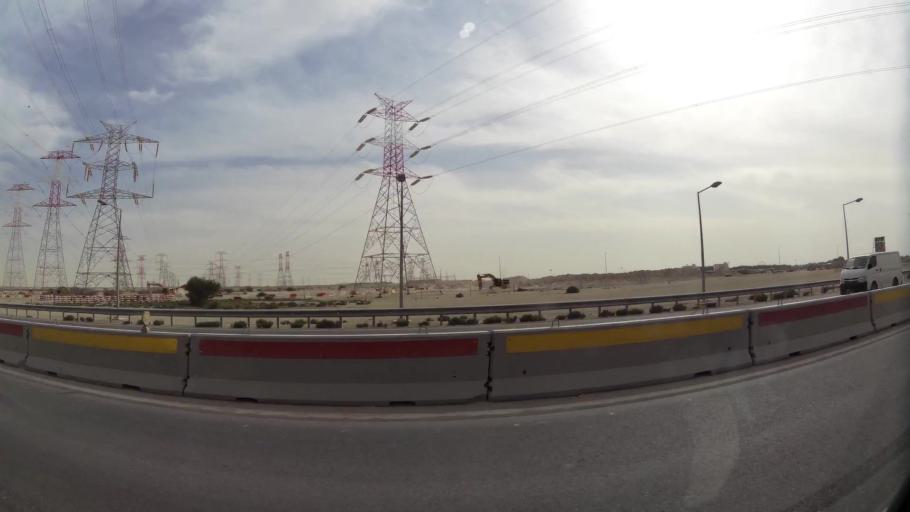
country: QA
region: Baladiyat ar Rayyan
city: Ash Shahaniyah
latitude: 25.3427
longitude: 51.3133
